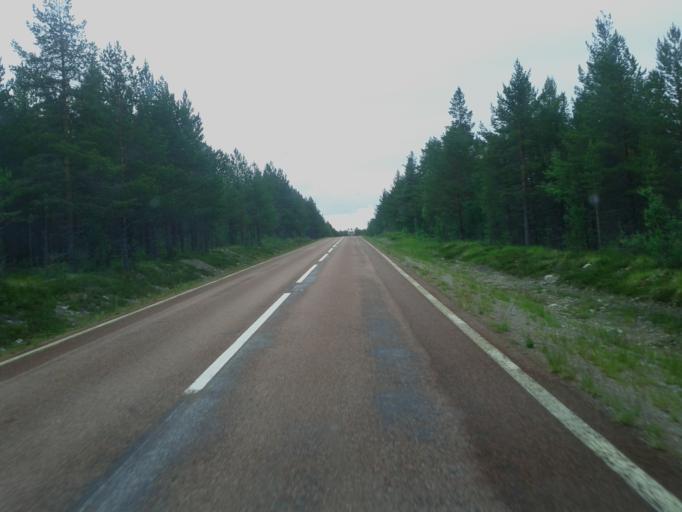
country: NO
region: Hedmark
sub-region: Engerdal
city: Engerdal
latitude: 61.8143
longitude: 12.3532
